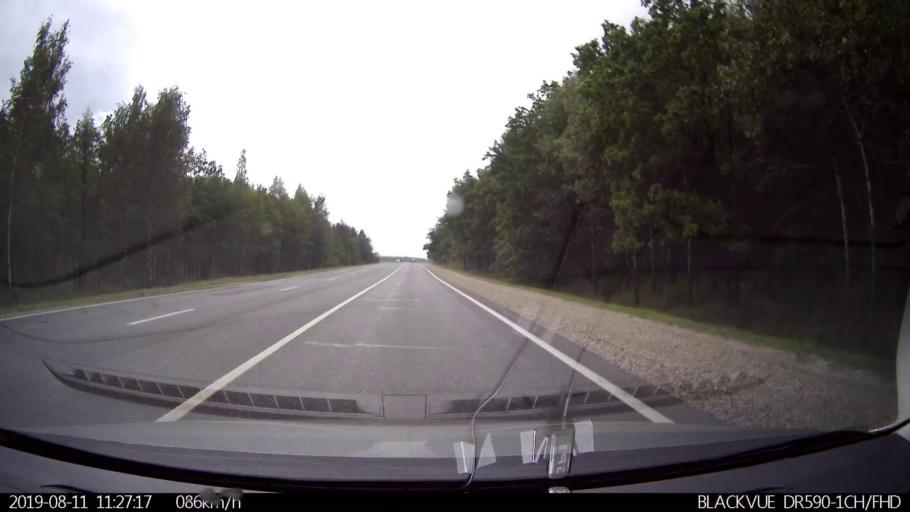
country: RU
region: Ulyanovsk
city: Krasnyy Gulyay
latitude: 54.0948
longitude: 48.2322
